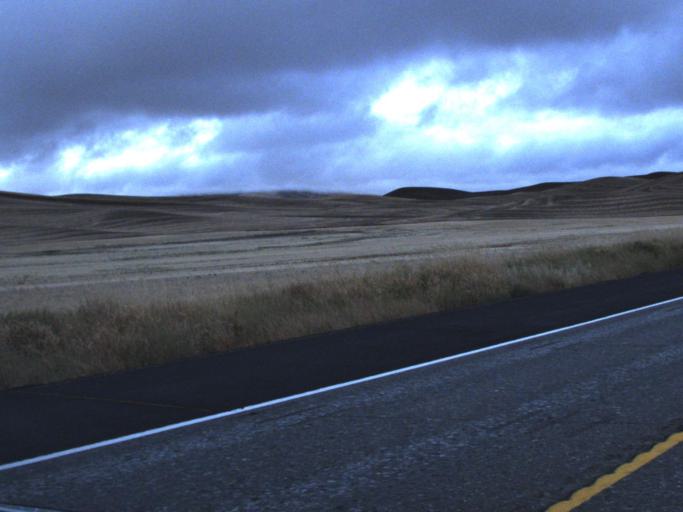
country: US
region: Washington
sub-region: Whitman County
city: Colfax
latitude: 47.0431
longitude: -117.3756
